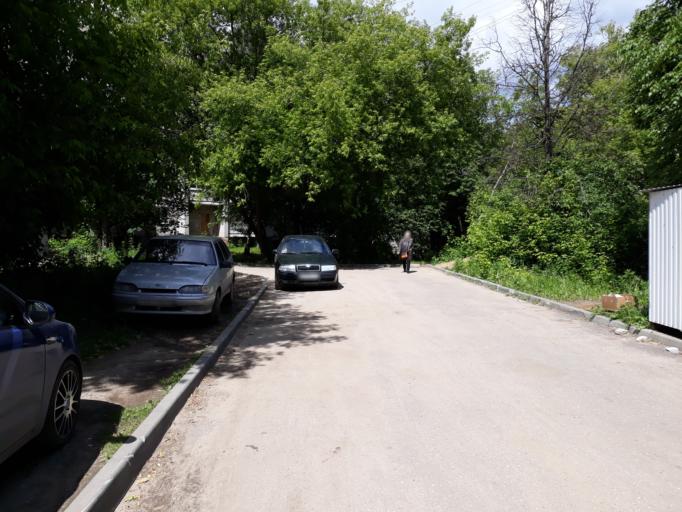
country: RU
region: Ivanovo
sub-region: Gorod Ivanovo
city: Ivanovo
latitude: 57.0078
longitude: 40.9861
